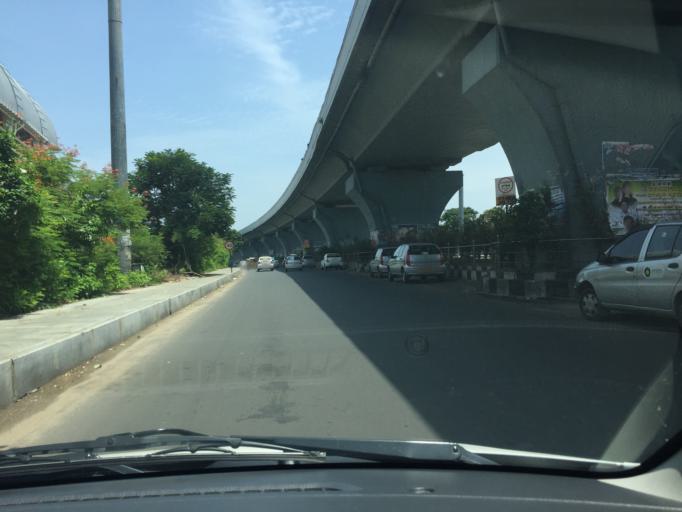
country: IN
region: Tamil Nadu
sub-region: Kancheepuram
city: Pallavaram
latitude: 12.9803
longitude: 80.1637
